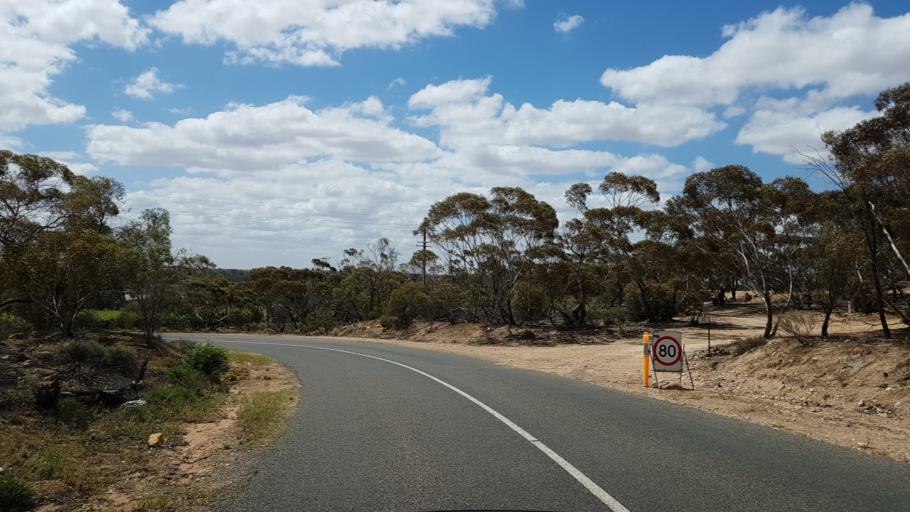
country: AU
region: South Australia
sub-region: Loxton Waikerie
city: Waikerie
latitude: -34.1851
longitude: 140.0187
